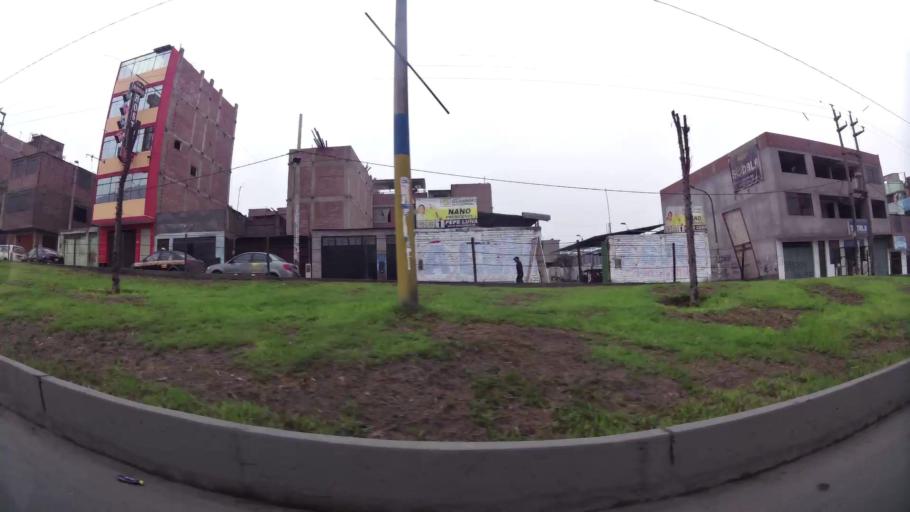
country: PE
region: Lima
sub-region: Lima
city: Independencia
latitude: -11.9421
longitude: -76.9810
